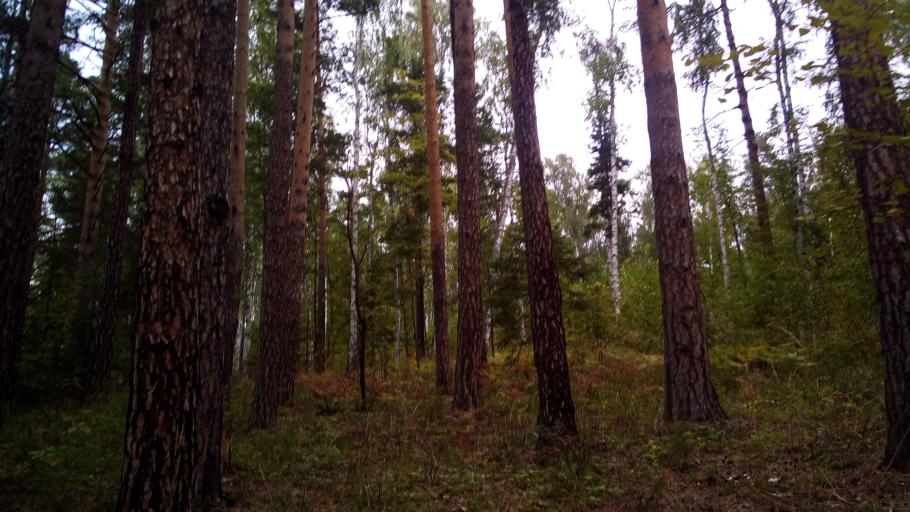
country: RU
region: Chelyabinsk
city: Turgoyak
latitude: 55.1818
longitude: 60.0292
